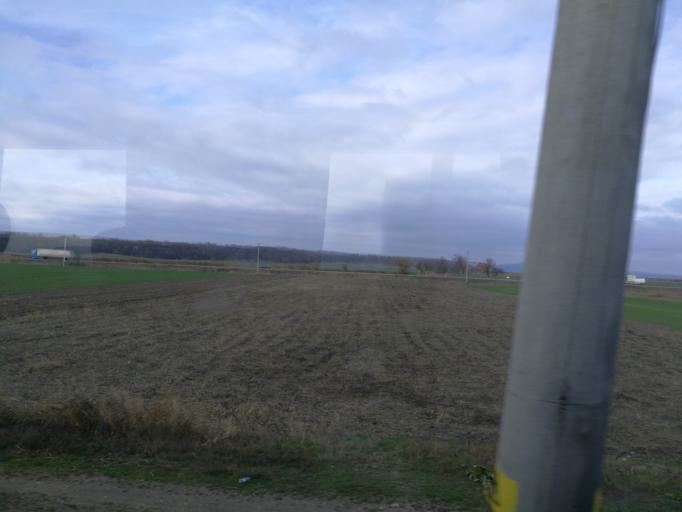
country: RO
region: Vrancea
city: Adjud
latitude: 46.0633
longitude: 27.1960
